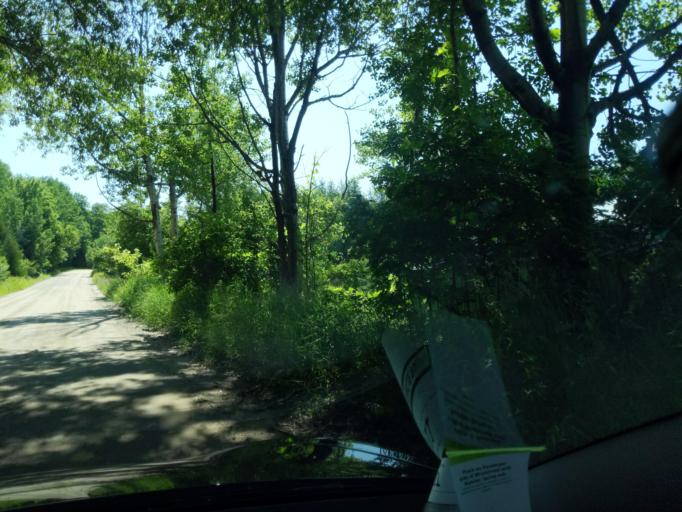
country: US
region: Michigan
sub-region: Cheboygan County
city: Cheboygan
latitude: 45.6501
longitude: -84.6219
